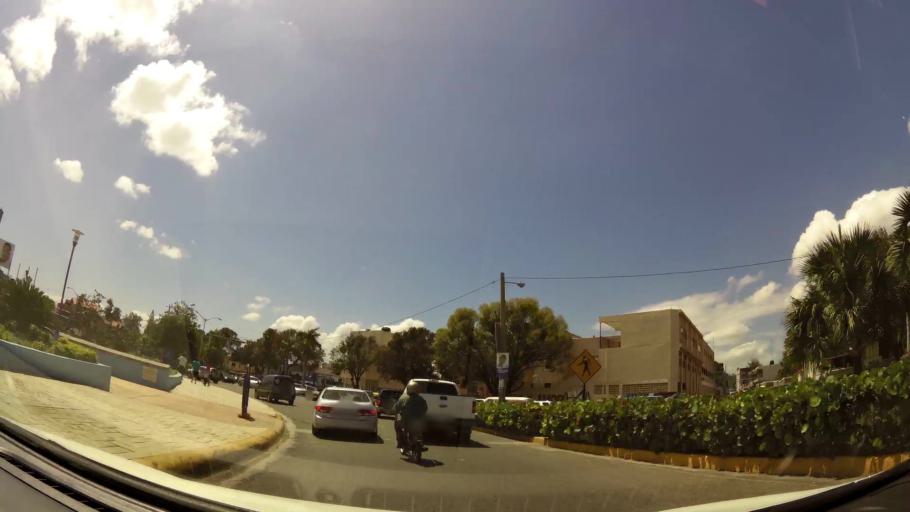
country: DO
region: San Cristobal
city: San Cristobal
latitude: 18.4170
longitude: -70.1076
